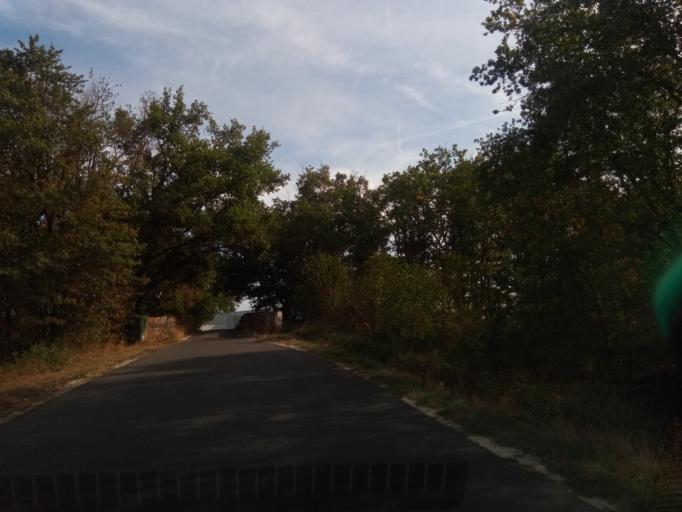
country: FR
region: Poitou-Charentes
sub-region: Departement de la Vienne
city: Saulge
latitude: 46.4041
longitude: 0.8888
